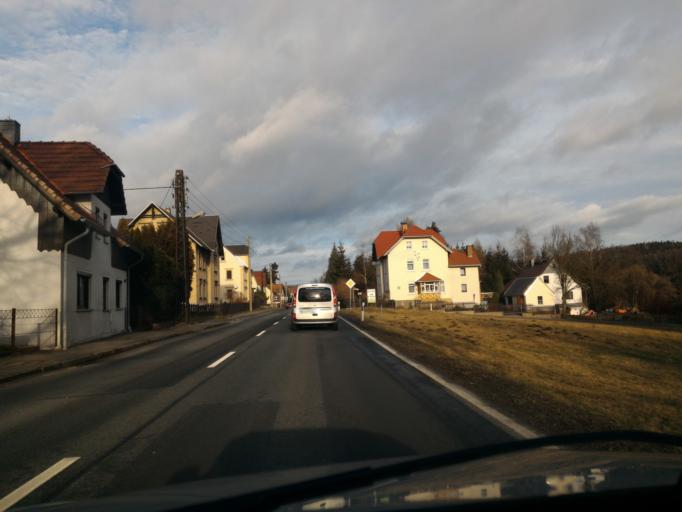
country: DE
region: Saxony
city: Friedersdorf
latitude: 51.0274
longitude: 14.5570
